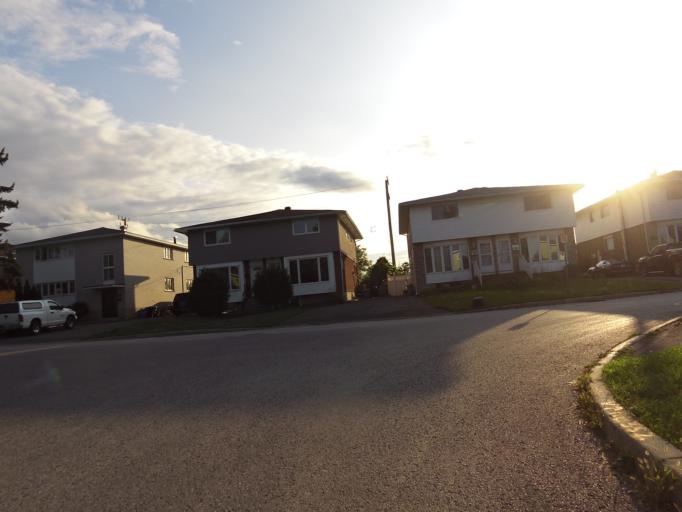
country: CA
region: Ontario
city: Ottawa
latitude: 45.3677
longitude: -75.7086
